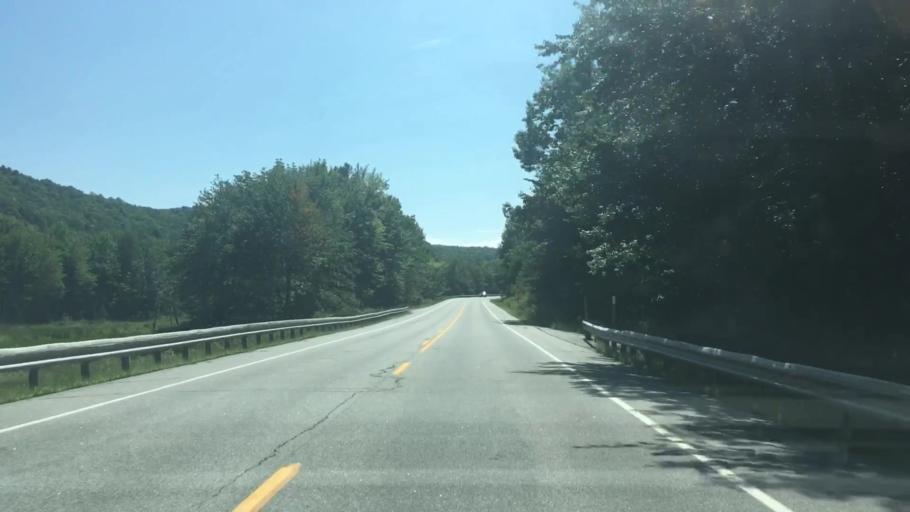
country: US
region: Maine
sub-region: Androscoggin County
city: Sabattus
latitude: 44.1520
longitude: -70.0360
